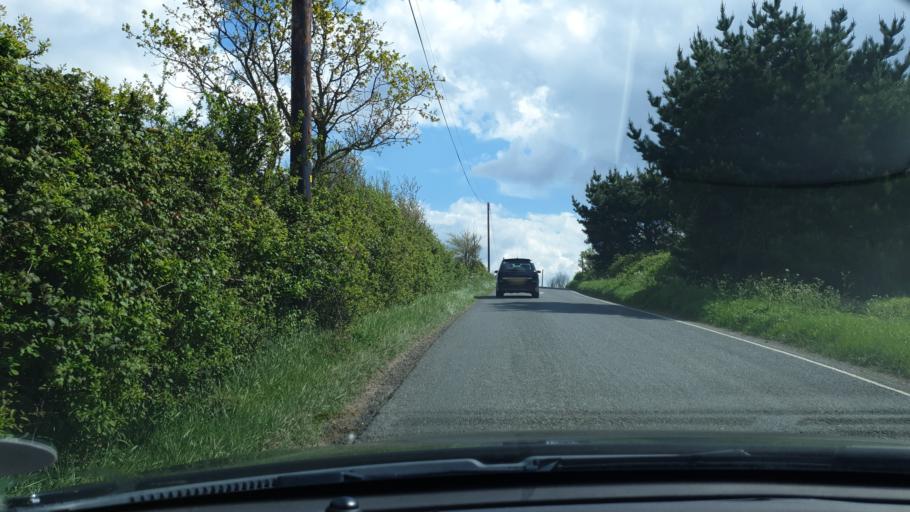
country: GB
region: England
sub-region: Essex
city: Frinton-on-Sea
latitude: 51.8590
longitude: 1.1996
